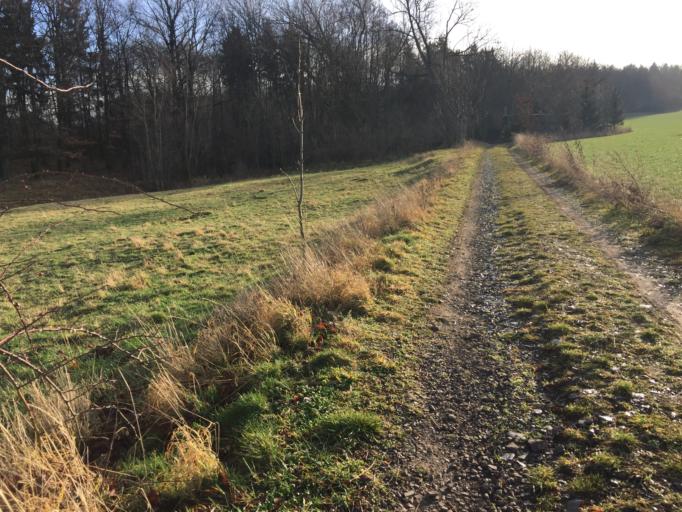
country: DE
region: Thuringia
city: Wernburg
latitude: 50.6667
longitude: 11.5914
